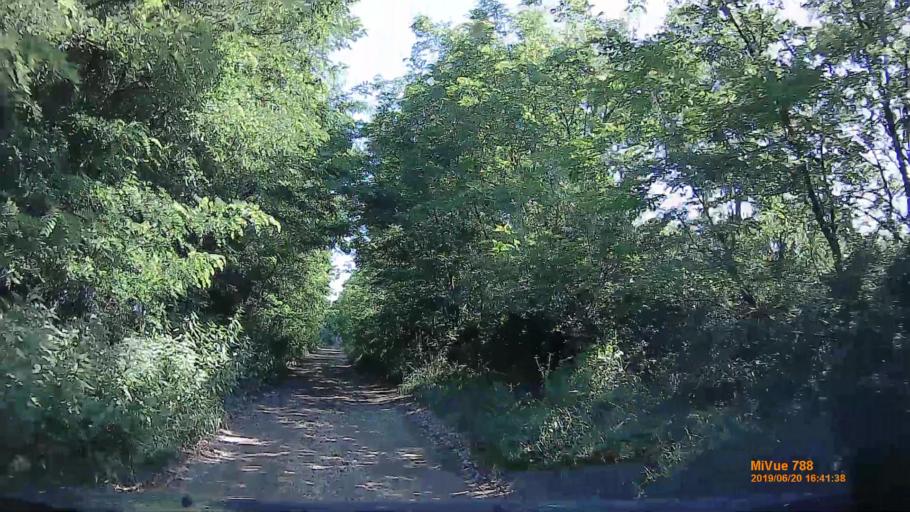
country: HU
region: Baranya
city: Buekkoesd
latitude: 46.1637
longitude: 18.0350
